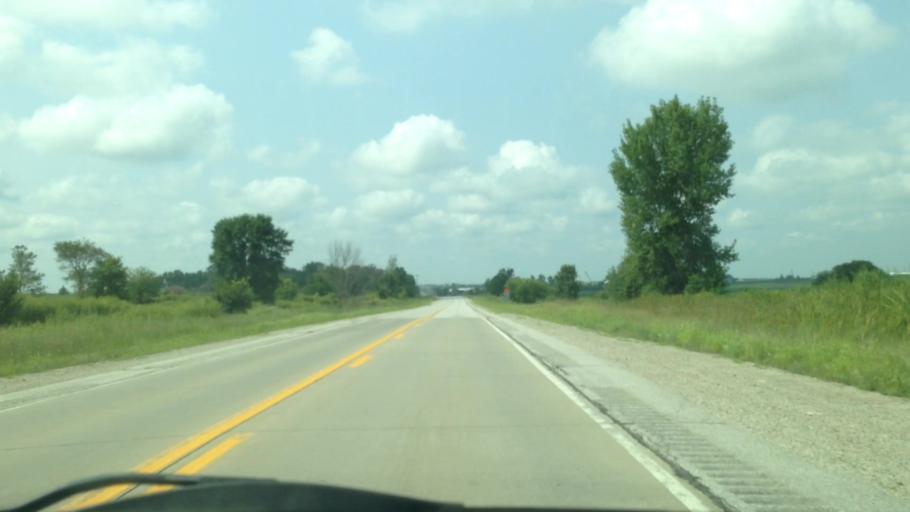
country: US
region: Iowa
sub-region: Benton County
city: Walford
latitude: 41.8973
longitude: -91.8081
